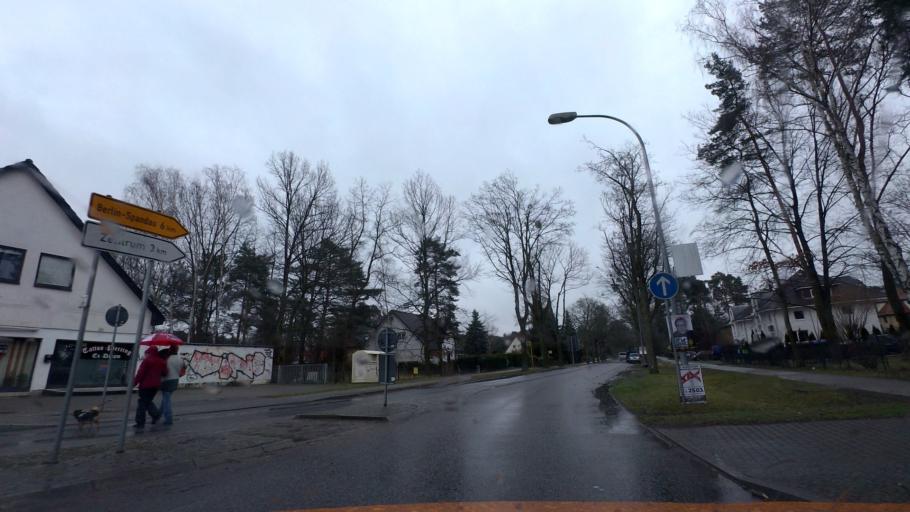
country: DE
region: Brandenburg
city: Falkensee
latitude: 52.5807
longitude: 13.0746
